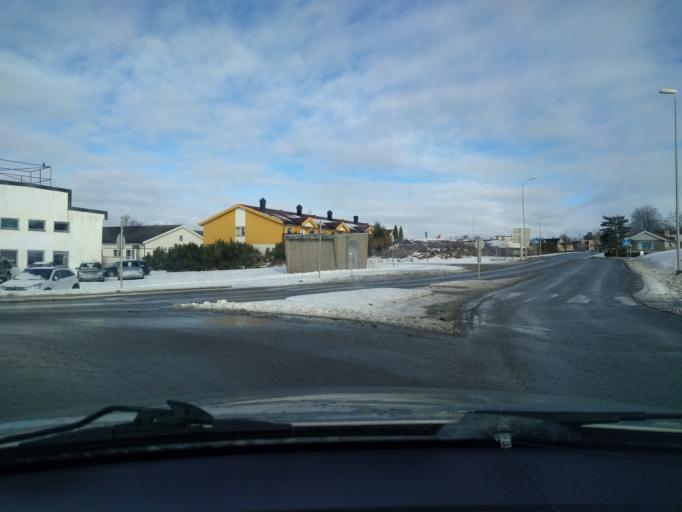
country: NO
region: Hedmark
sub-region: Hamar
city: Hamar
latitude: 60.7820
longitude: 11.1111
